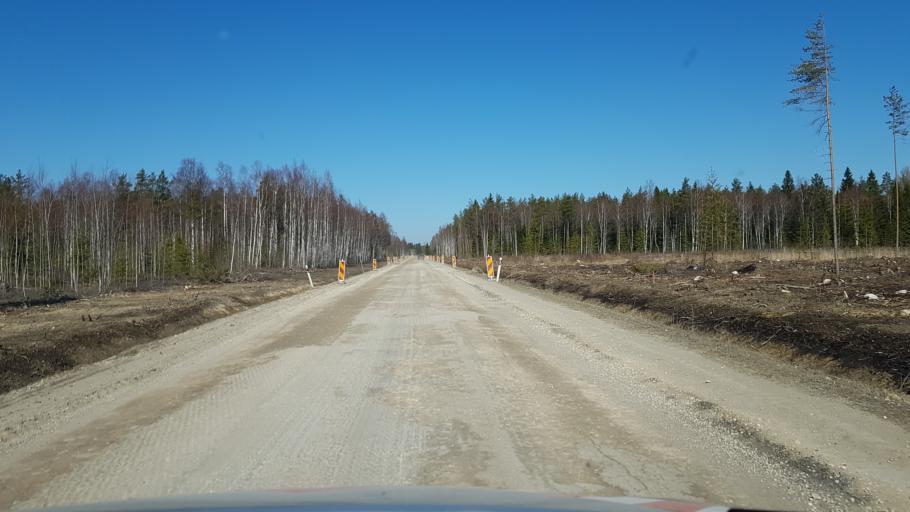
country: EE
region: Laeaene-Virumaa
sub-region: Vinni vald
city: Vinni
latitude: 59.0489
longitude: 26.6572
